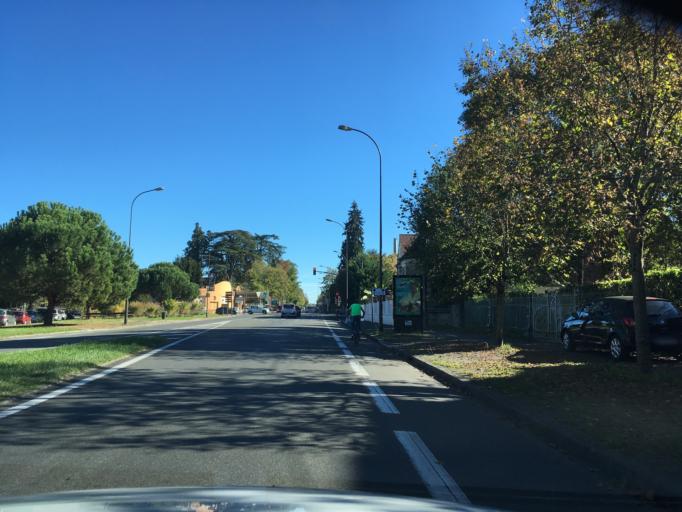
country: FR
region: Aquitaine
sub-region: Departement des Pyrenees-Atlantiques
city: Pau
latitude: 43.3023
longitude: -0.3534
